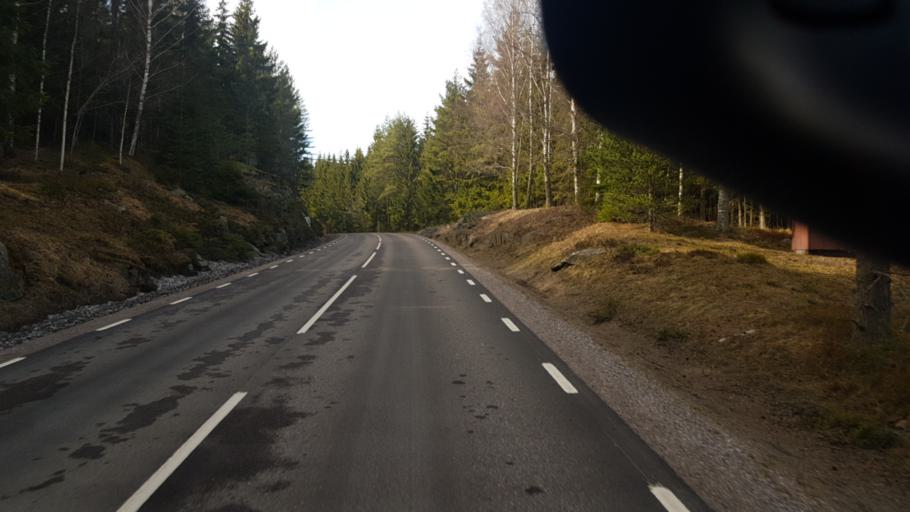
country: SE
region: Vaermland
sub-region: Eda Kommun
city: Amotfors
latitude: 59.7355
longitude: 12.4081
